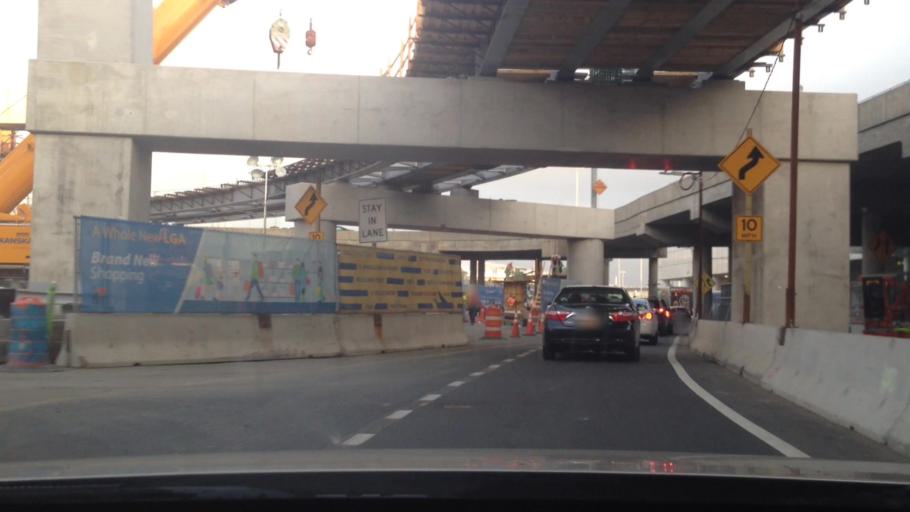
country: US
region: New York
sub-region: Bronx
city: The Bronx
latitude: 40.7707
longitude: -73.8658
